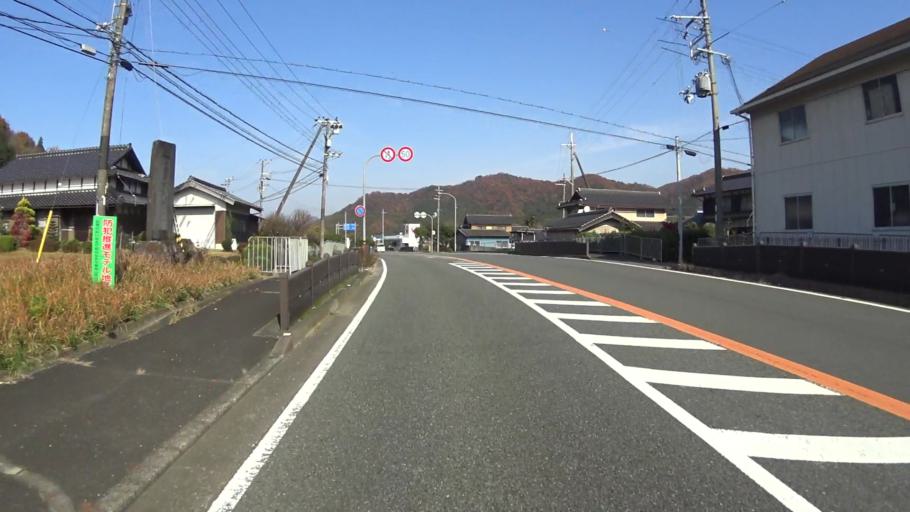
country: JP
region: Kyoto
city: Ayabe
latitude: 35.2267
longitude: 135.2262
